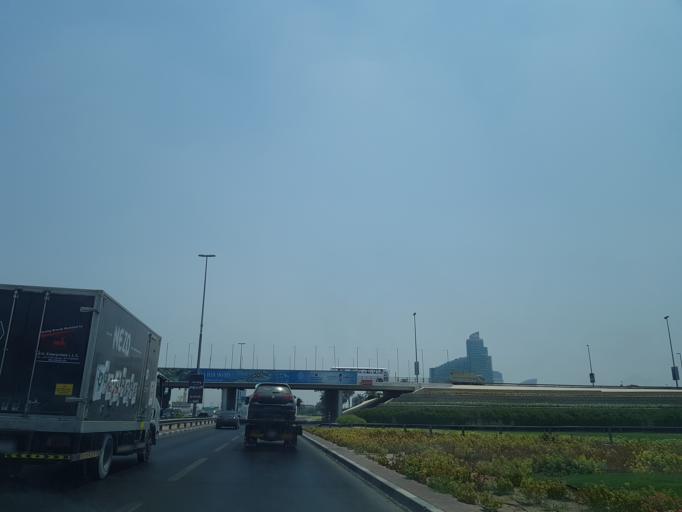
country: AE
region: Ash Shariqah
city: Sharjah
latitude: 25.2386
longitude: 55.3429
